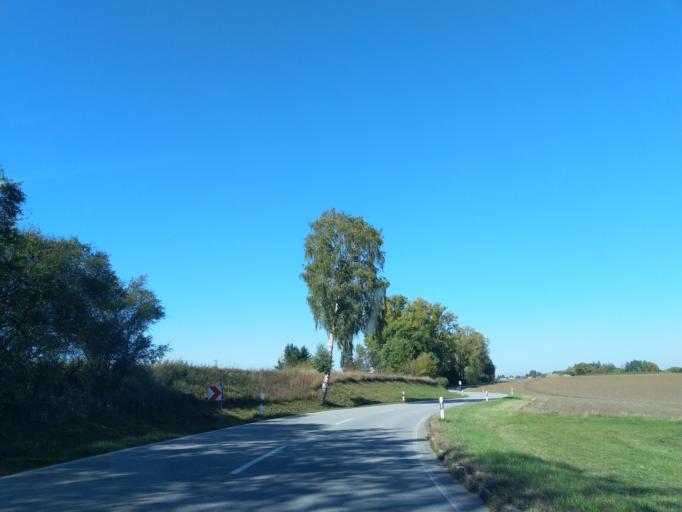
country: DE
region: Bavaria
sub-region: Lower Bavaria
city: Stephansposching
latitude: 48.8176
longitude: 12.7942
